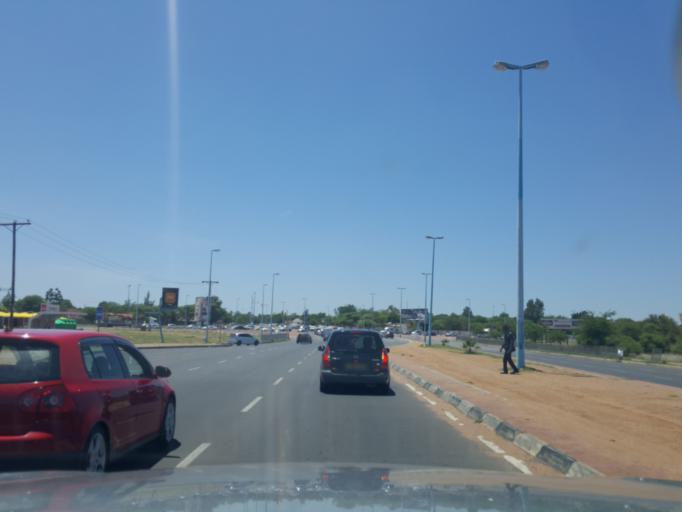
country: BW
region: Kweneng
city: Mogoditshane
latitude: -24.6442
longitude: 25.8834
